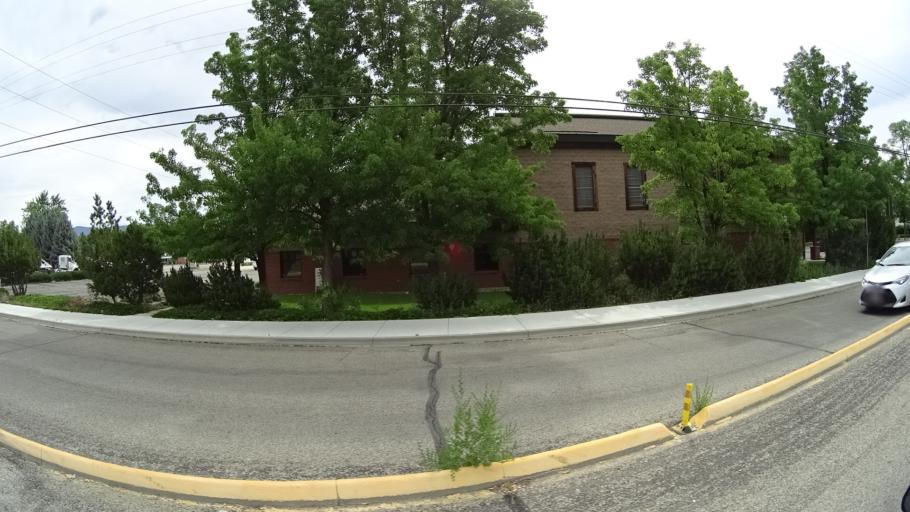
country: US
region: Idaho
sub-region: Ada County
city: Boise
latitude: 43.5894
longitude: -116.2237
